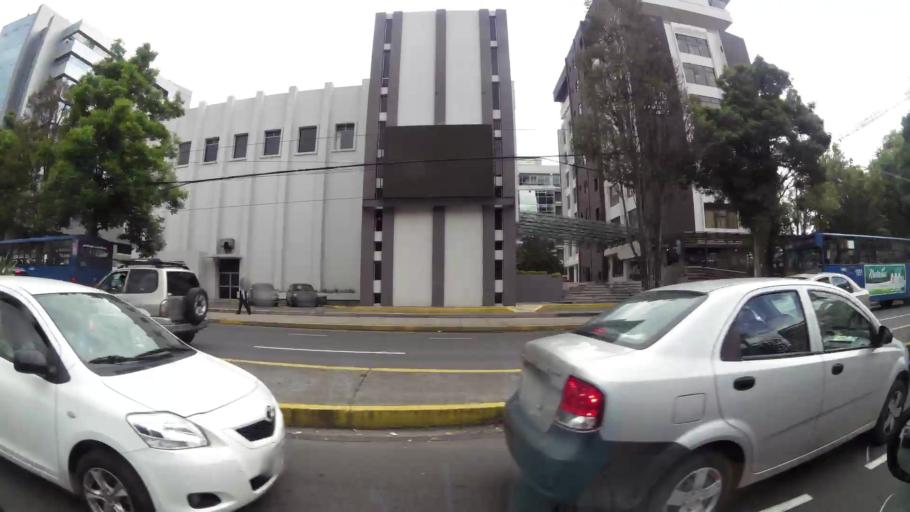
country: EC
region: Pichincha
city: Quito
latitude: -0.1734
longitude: -78.4852
